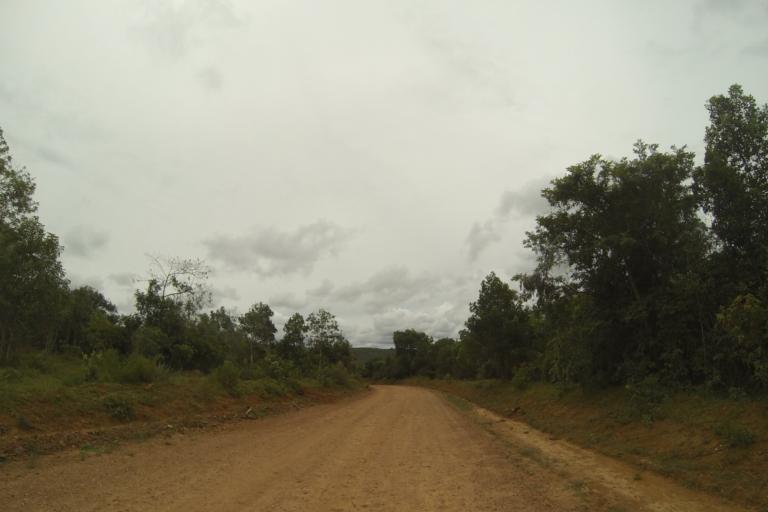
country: BR
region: Minas Gerais
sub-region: Ibia
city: Ibia
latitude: -19.6628
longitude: -46.7017
